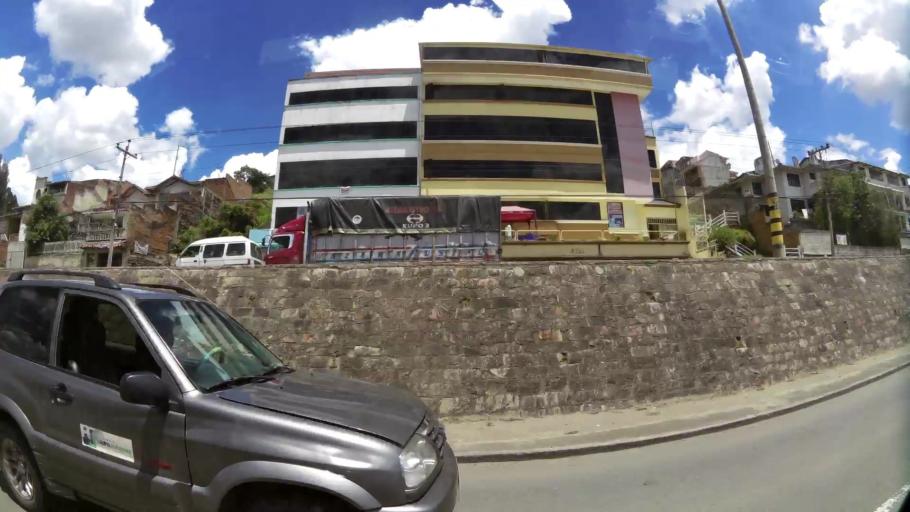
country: EC
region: Azuay
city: Cuenca
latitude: -2.8890
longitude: -79.0144
